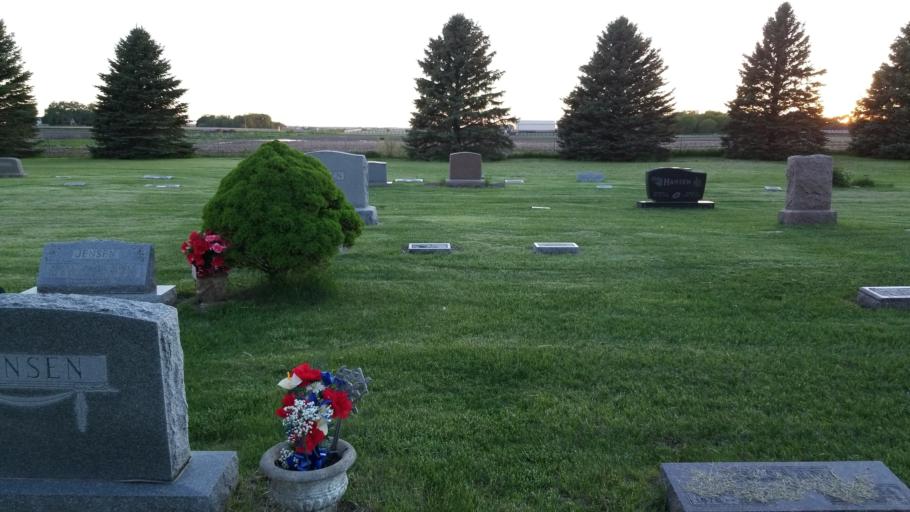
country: US
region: South Dakota
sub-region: Union County
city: Beresford
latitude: 42.9396
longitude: -96.8306
